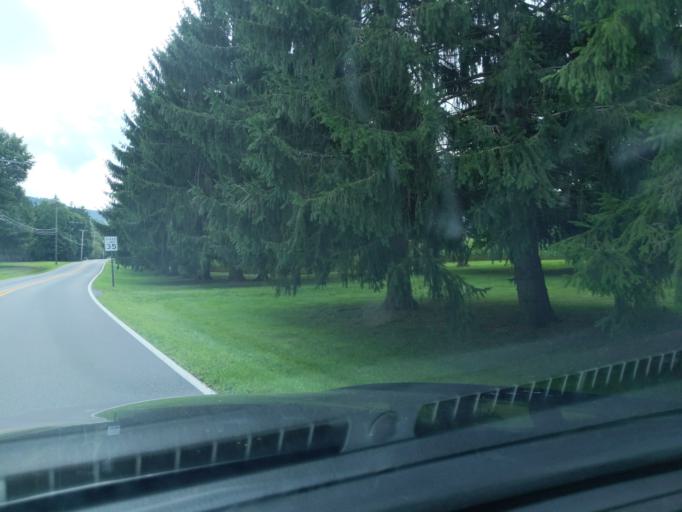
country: US
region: Pennsylvania
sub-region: Blair County
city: Hollidaysburg
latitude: 40.3952
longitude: -78.4040
